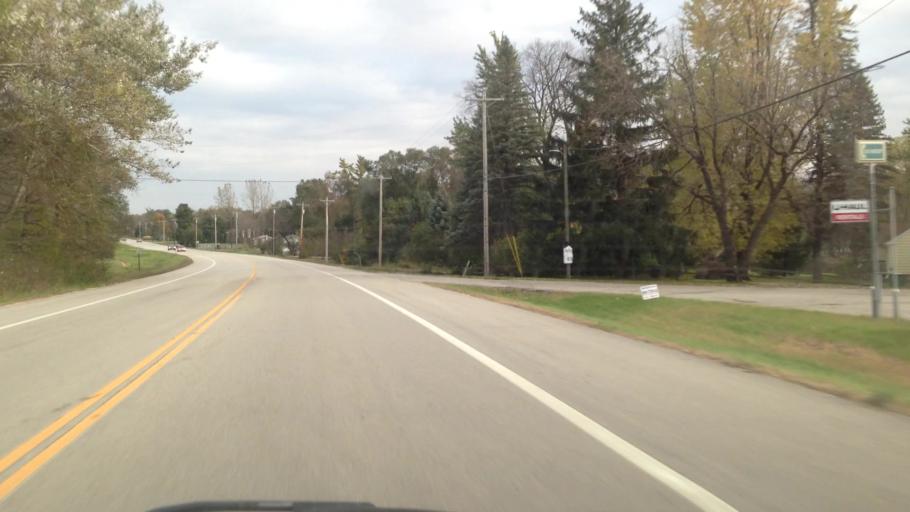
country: US
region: Minnesota
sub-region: Olmsted County
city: Rochester
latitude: 43.9740
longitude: -92.3927
